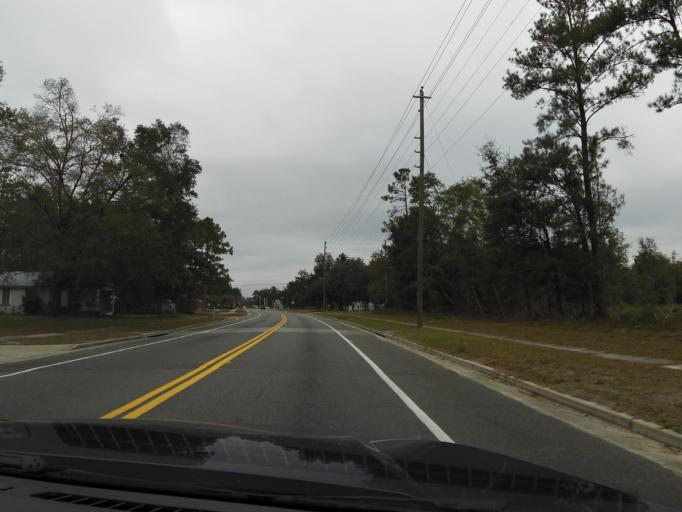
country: US
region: Georgia
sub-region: Charlton County
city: Folkston
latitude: 30.8277
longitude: -82.0093
